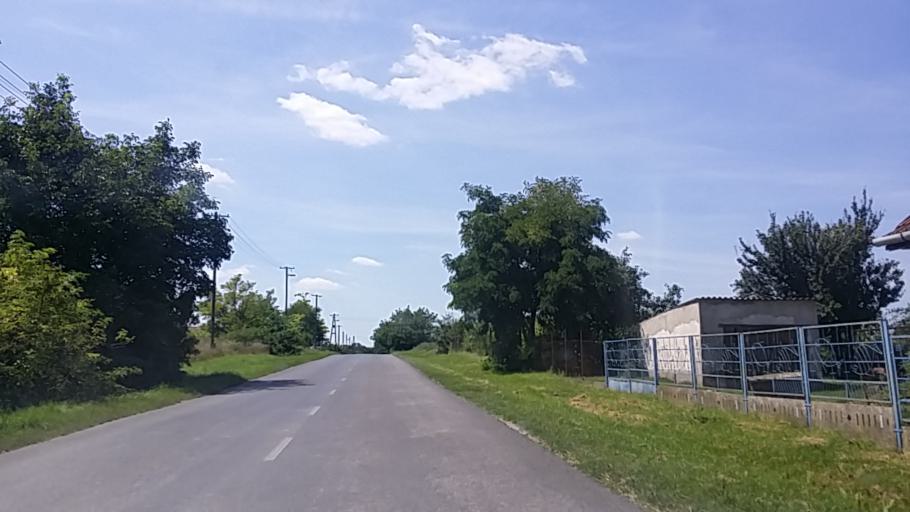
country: HU
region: Fejer
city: Deg
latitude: 46.8545
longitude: 18.4033
